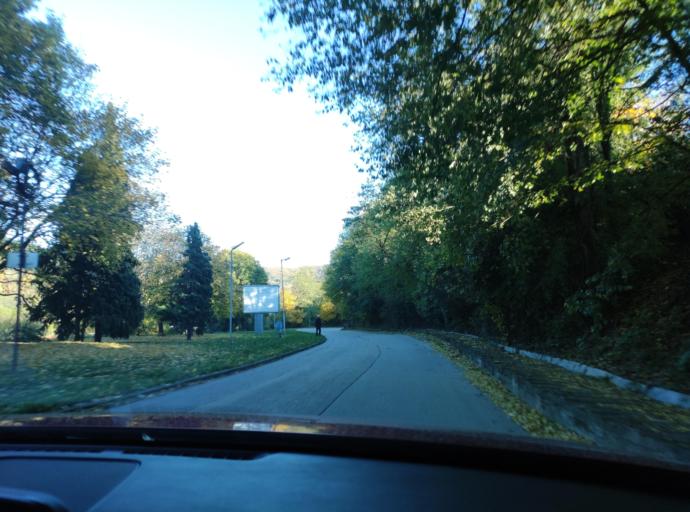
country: BG
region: Montana
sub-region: Obshtina Chiprovtsi
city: Chiprovtsi
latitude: 43.3836
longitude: 22.8908
